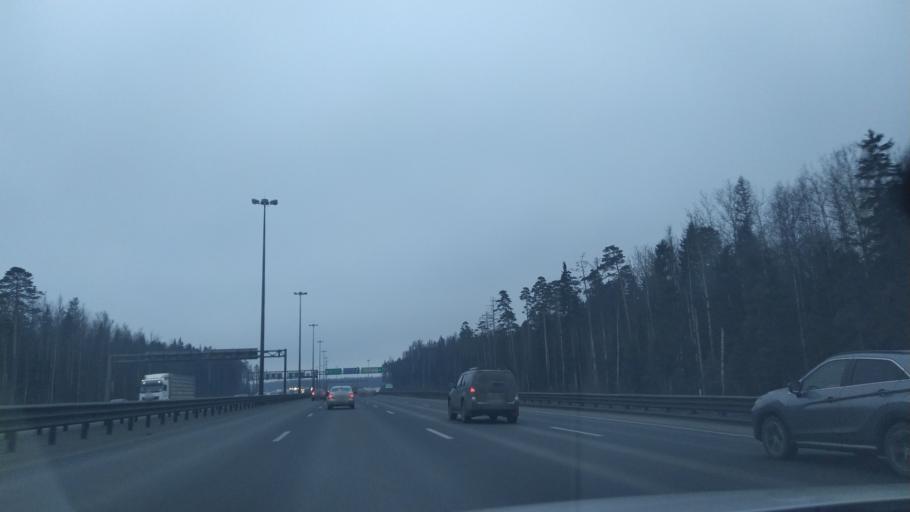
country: RU
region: Leningrad
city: Yanino Vtoroye
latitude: 59.9536
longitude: 30.5476
